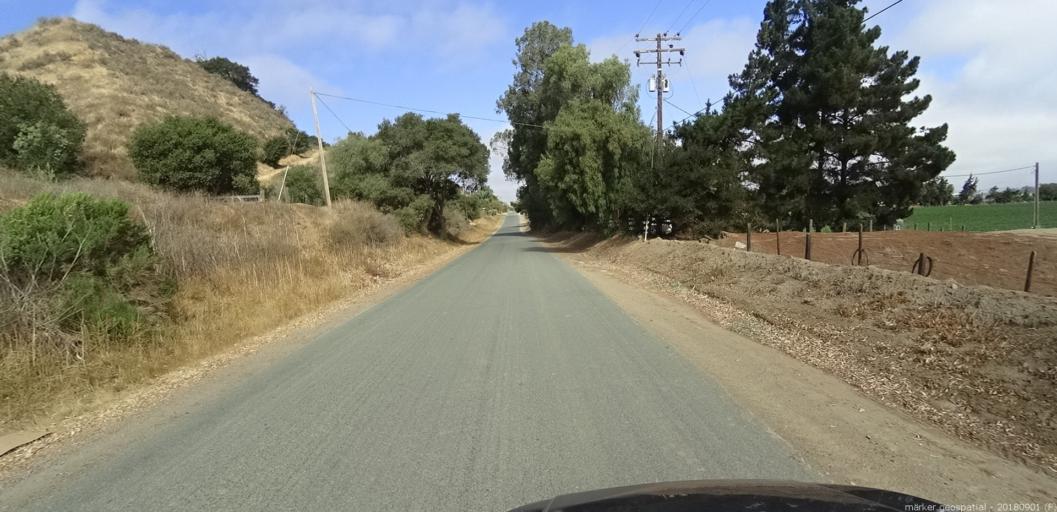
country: US
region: California
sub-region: Monterey County
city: Soledad
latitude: 36.3855
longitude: -121.3589
